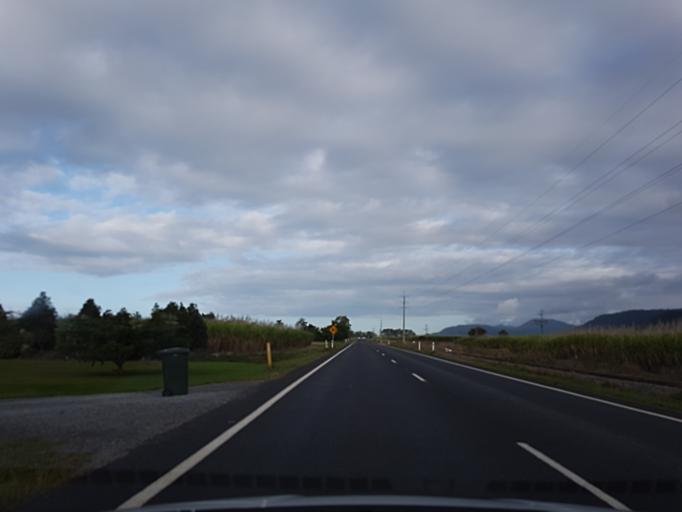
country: AU
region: Queensland
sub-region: Cairns
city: Port Douglas
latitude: -16.5014
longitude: 145.4331
